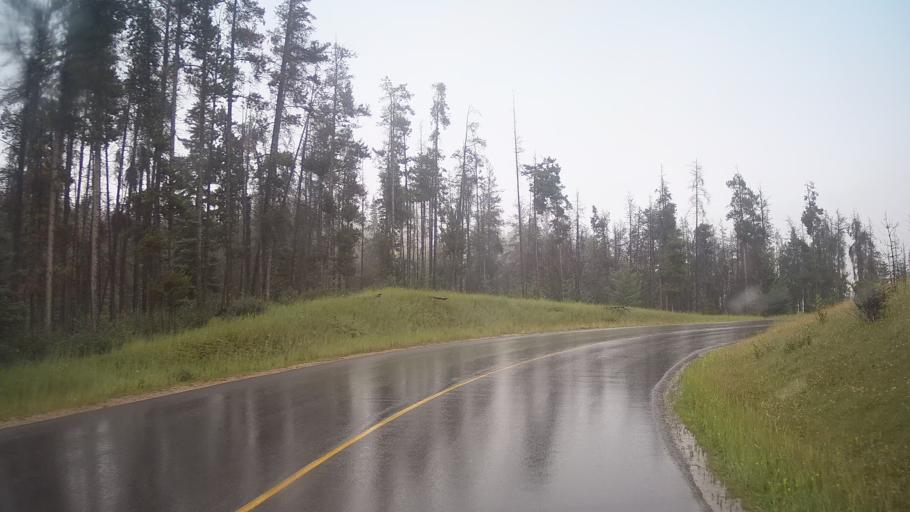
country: CA
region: Alberta
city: Jasper Park Lodge
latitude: 52.8915
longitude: -118.0831
